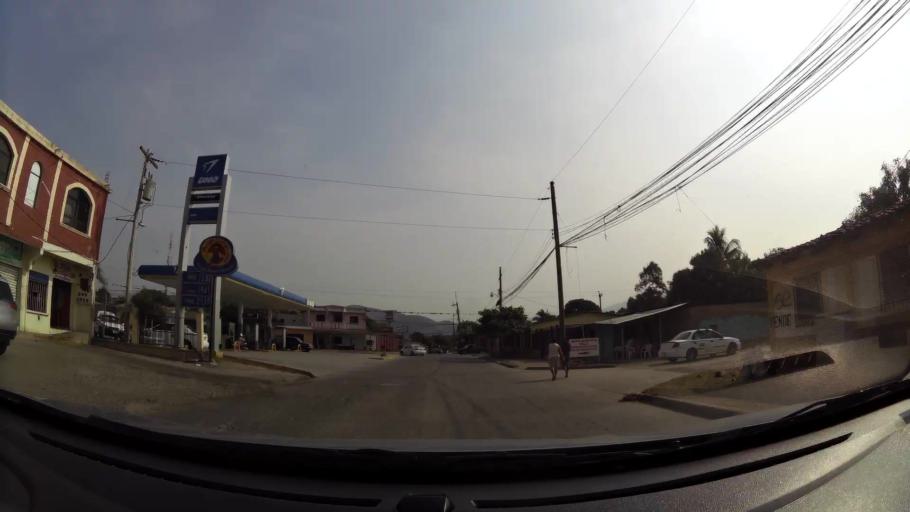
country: HN
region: Comayagua
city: Comayagua
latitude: 14.4563
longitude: -87.6292
